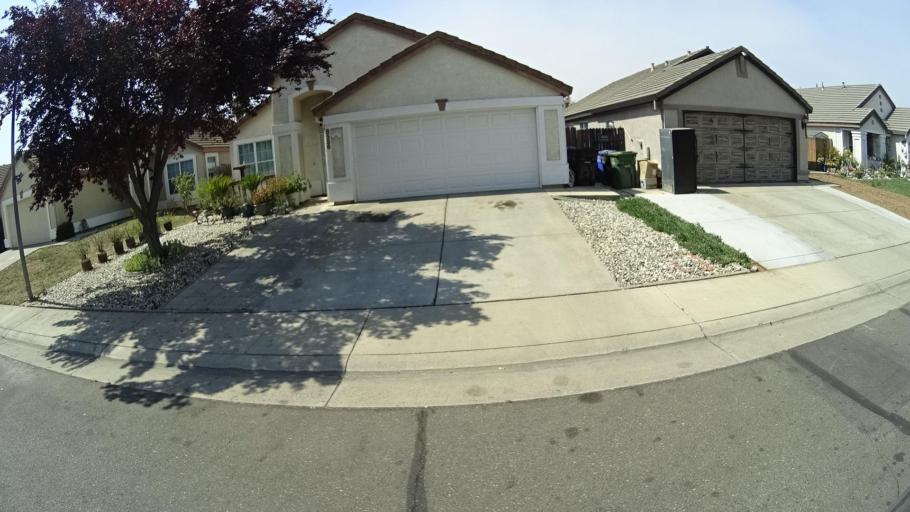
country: US
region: California
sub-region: Sacramento County
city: Vineyard
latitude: 38.4464
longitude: -121.3750
